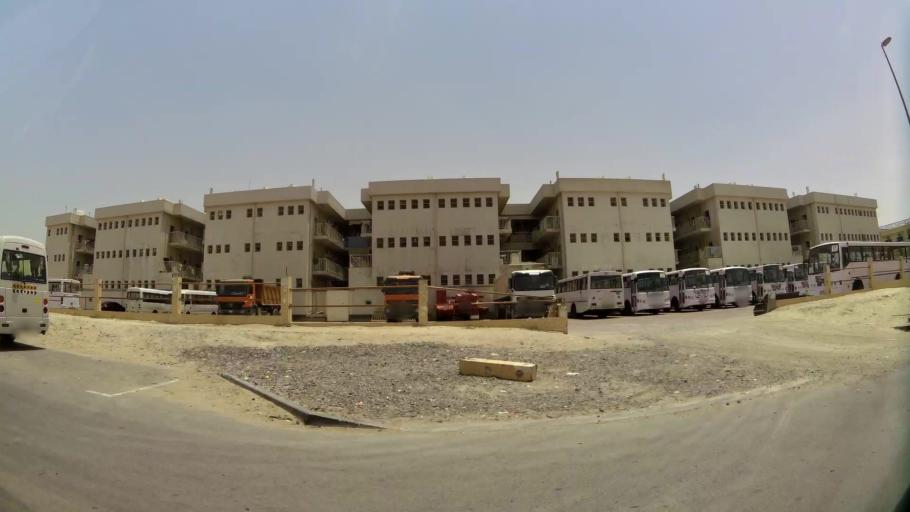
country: AE
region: Ash Shariqah
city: Sharjah
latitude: 25.2753
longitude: 55.4229
